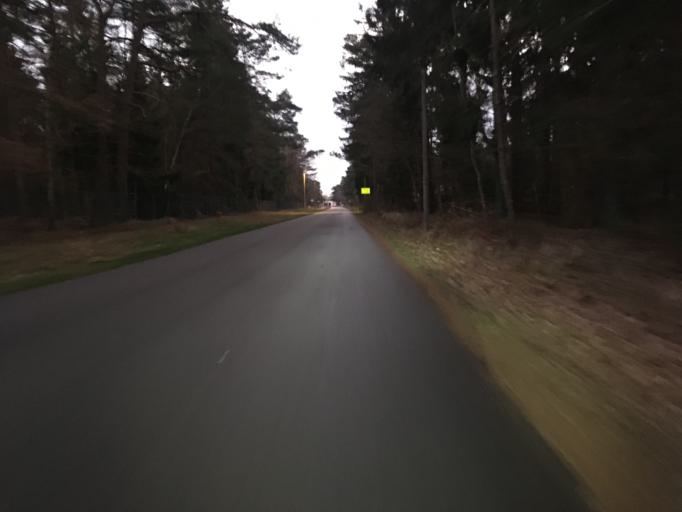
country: DE
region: Mecklenburg-Vorpommern
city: Ostseebad Binz
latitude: 54.4496
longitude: 13.5651
